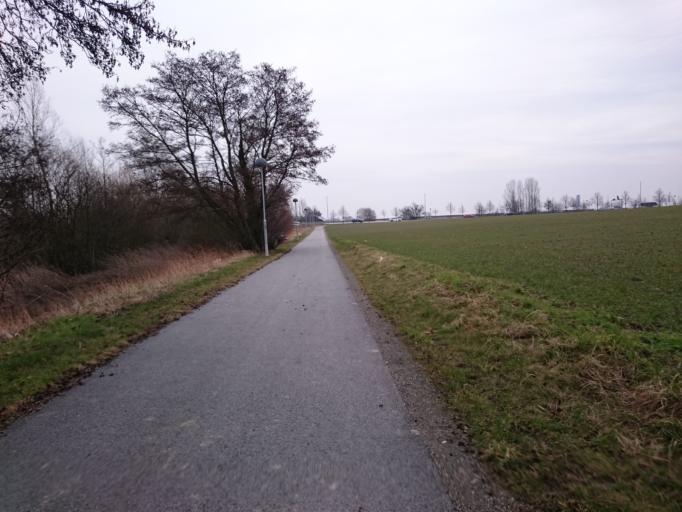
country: SE
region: Skane
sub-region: Lunds Kommun
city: Lund
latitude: 55.6822
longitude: 13.1820
